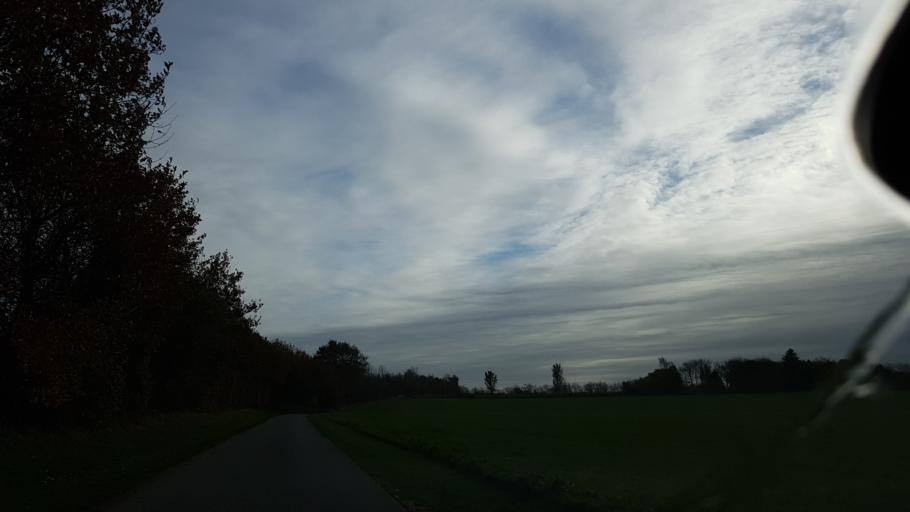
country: DK
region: South Denmark
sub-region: Haderslev Kommune
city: Gram
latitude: 55.2585
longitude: 9.1200
